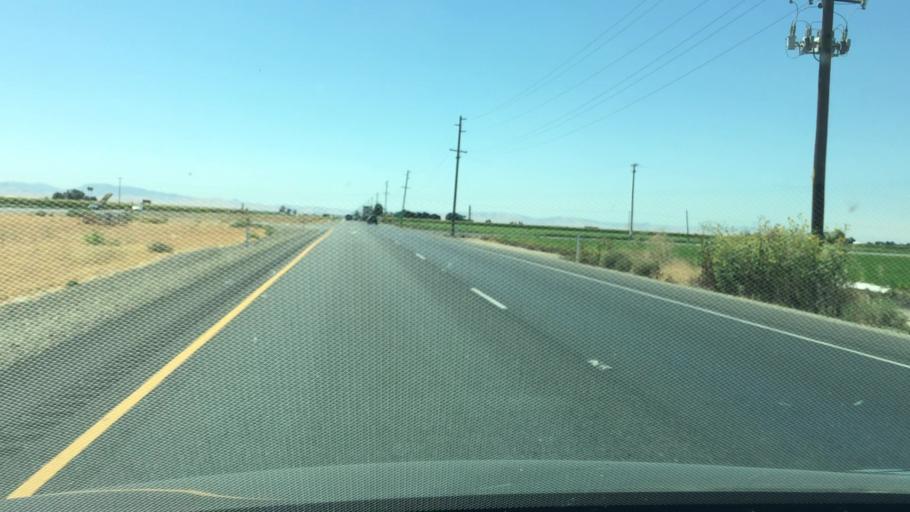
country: US
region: California
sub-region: Merced County
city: Dos Palos
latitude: 37.0548
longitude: -120.7044
